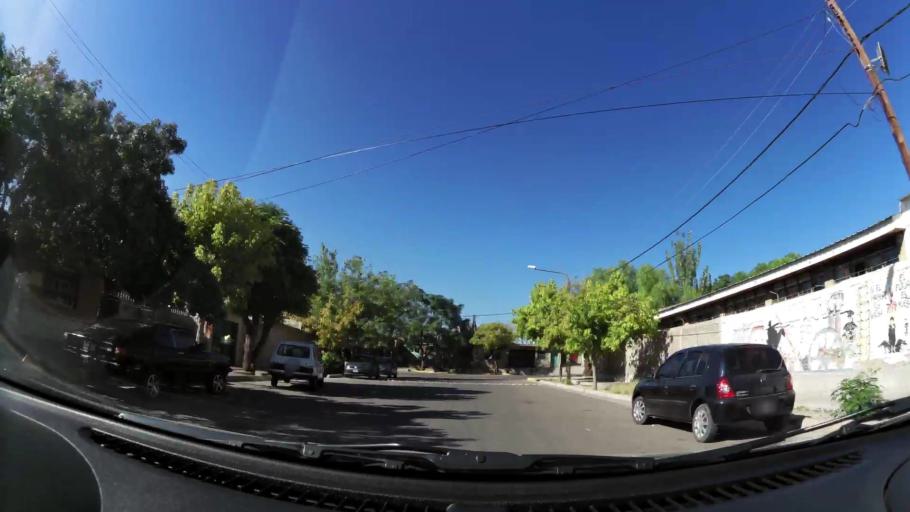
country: AR
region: Mendoza
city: Mendoza
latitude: -32.8743
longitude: -68.8692
